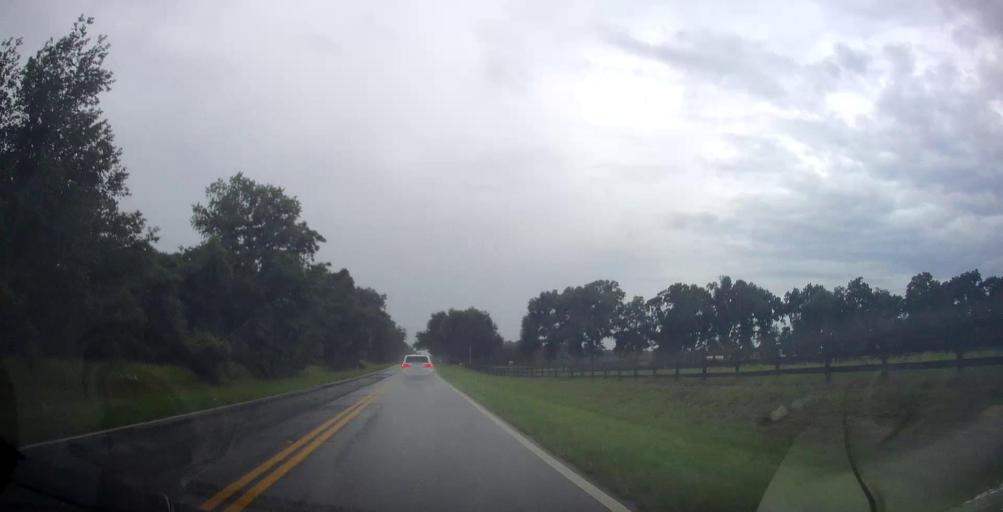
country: US
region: Florida
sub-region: Marion County
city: Ocala
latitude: 29.2476
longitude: -82.0891
